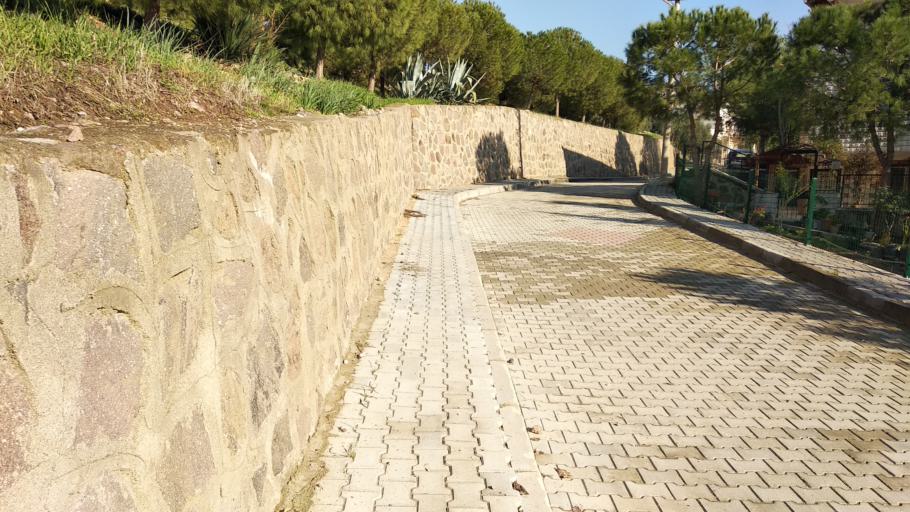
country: TR
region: Izmir
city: Karsiyaka
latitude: 38.4962
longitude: 27.0801
